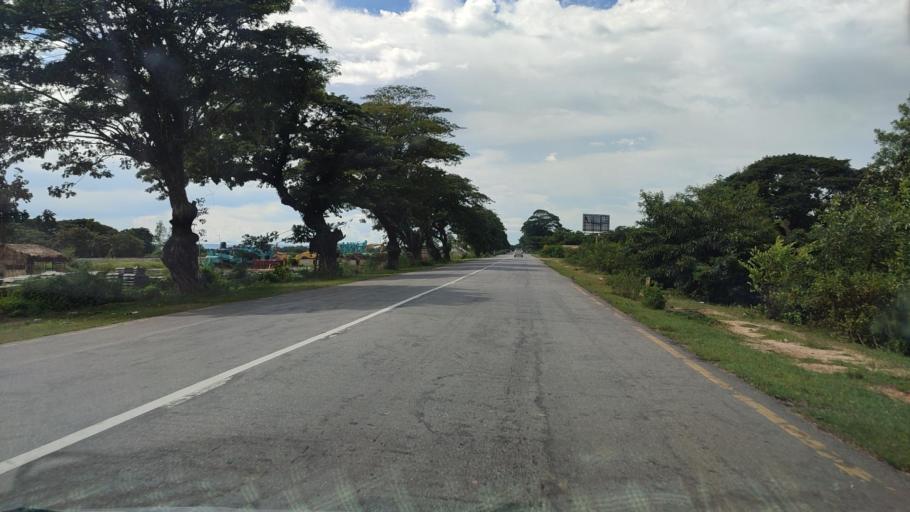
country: MM
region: Bago
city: Nyaunglebin
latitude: 18.1705
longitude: 96.6017
